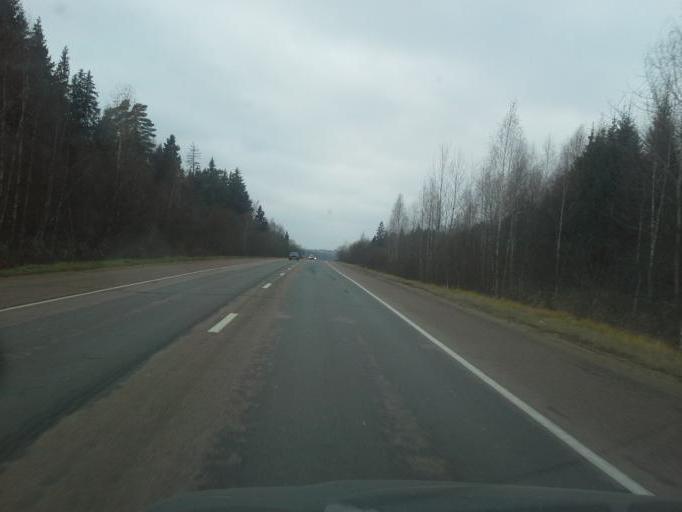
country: RU
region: Moskovskaya
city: Solnechnogorsk
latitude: 56.1415
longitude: 36.9698
